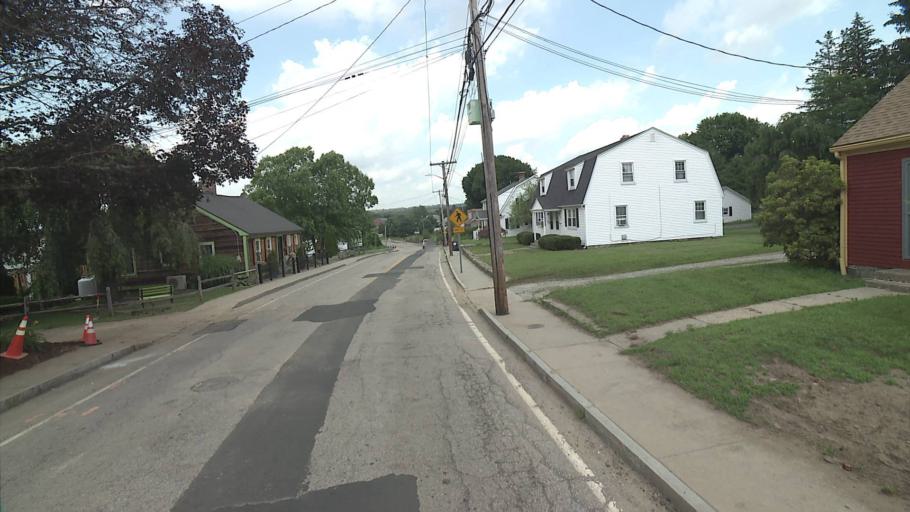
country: US
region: Connecticut
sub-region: New London County
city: Jewett City
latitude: 41.6021
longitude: -71.9821
